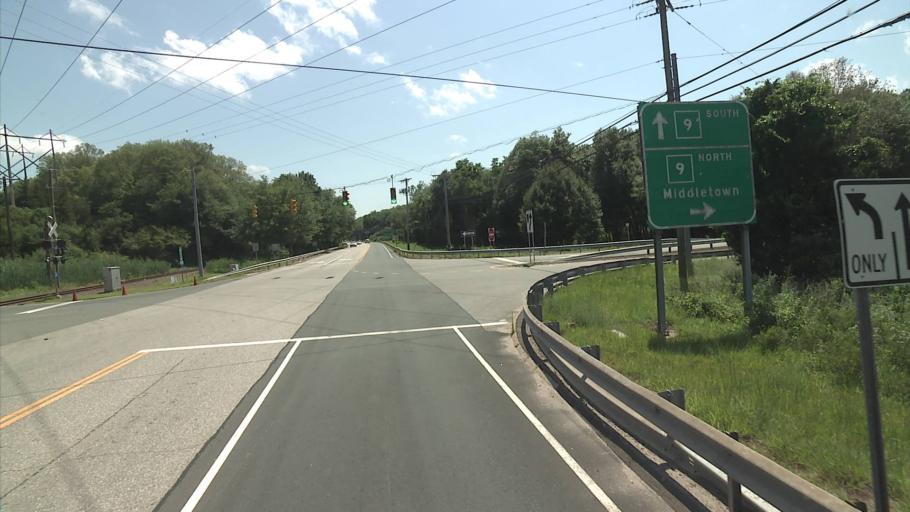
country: US
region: Connecticut
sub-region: Middlesex County
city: Deep River Center
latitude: 41.3647
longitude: -72.4245
